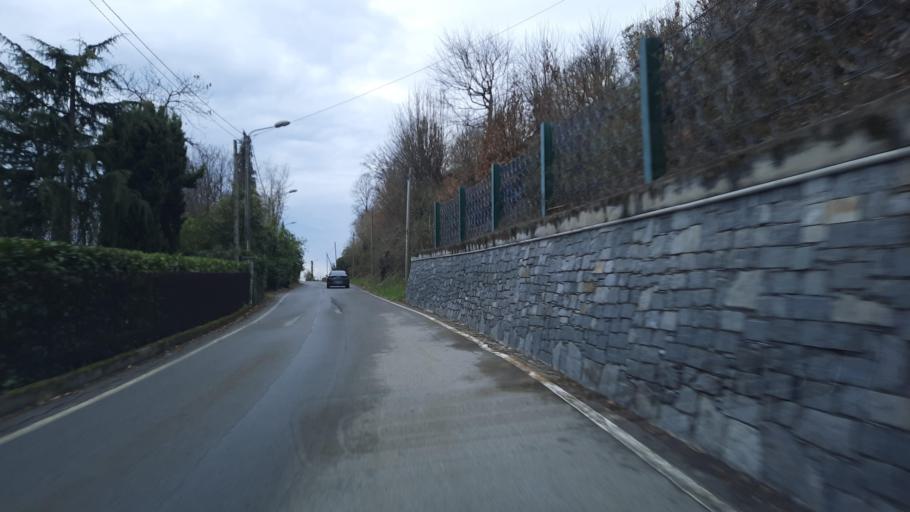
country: IT
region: Piedmont
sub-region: Provincia di Novara
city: Pella
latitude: 45.8079
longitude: 8.3847
